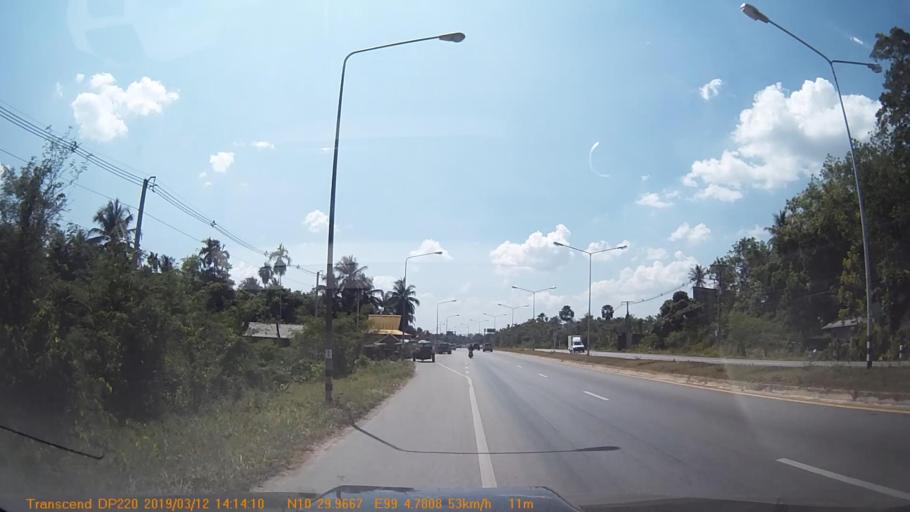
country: TH
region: Chumphon
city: Chumphon
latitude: 10.4995
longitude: 99.0794
